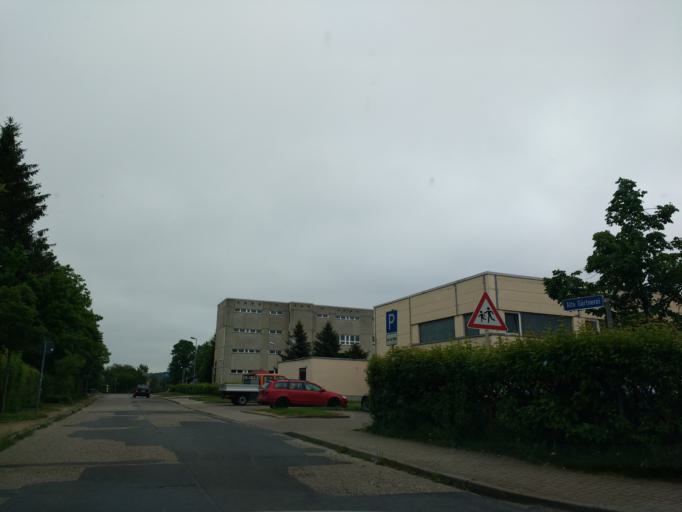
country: DE
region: Mecklenburg-Vorpommern
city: Neukloster
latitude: 53.8622
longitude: 11.6920
